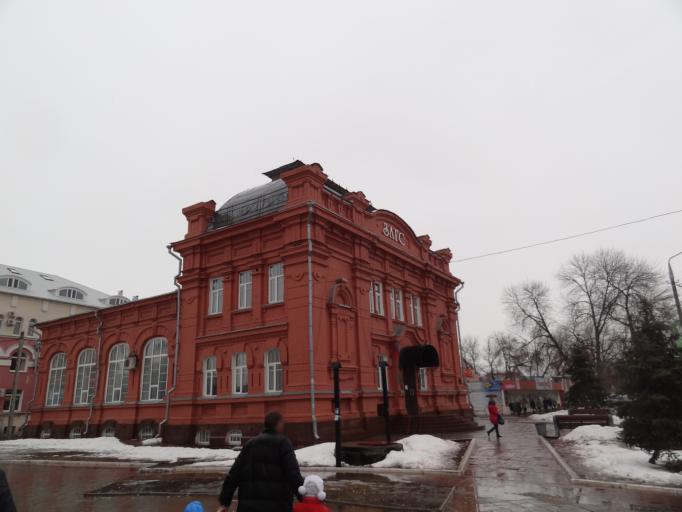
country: RU
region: Saratov
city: Engel's
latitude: 51.5001
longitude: 46.1260
